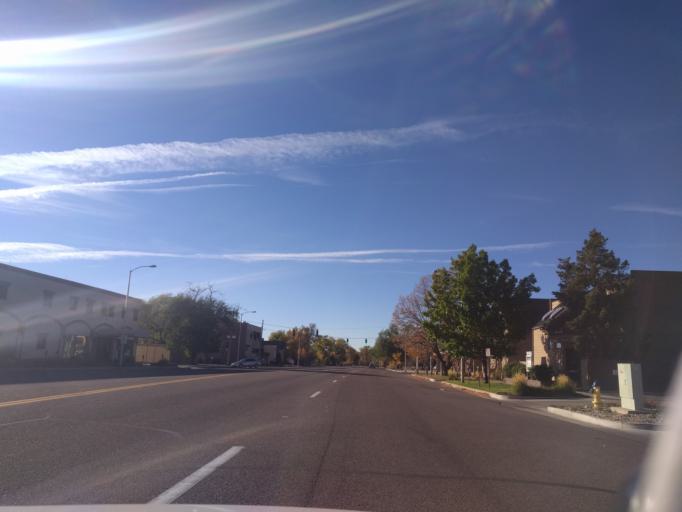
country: US
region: Colorado
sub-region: El Paso County
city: Colorado Springs
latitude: 38.8292
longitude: -104.8257
